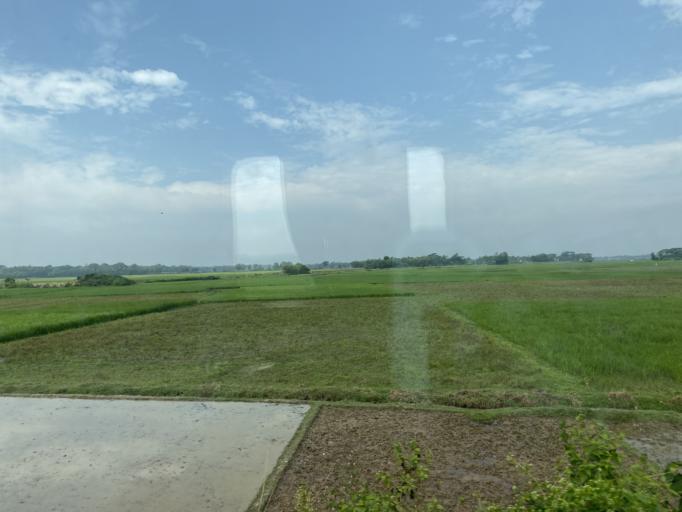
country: IN
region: Tripura
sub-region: West Tripura
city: Agartala
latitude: 23.9924
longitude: 91.2861
